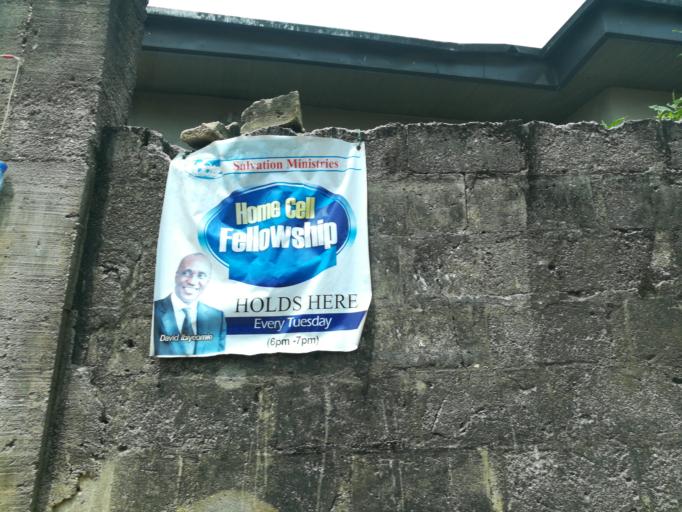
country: NG
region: Rivers
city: Port Harcourt
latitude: 4.8916
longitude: 6.9818
